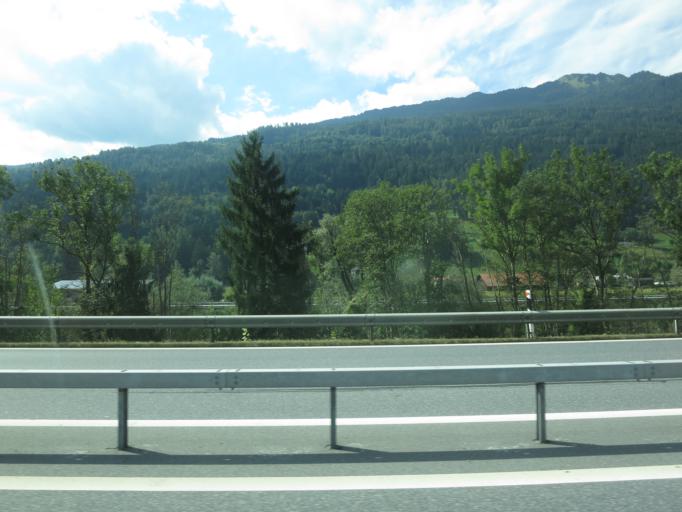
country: CH
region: Grisons
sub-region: Hinterrhein District
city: Cazis
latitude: 46.7555
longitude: 9.4266
